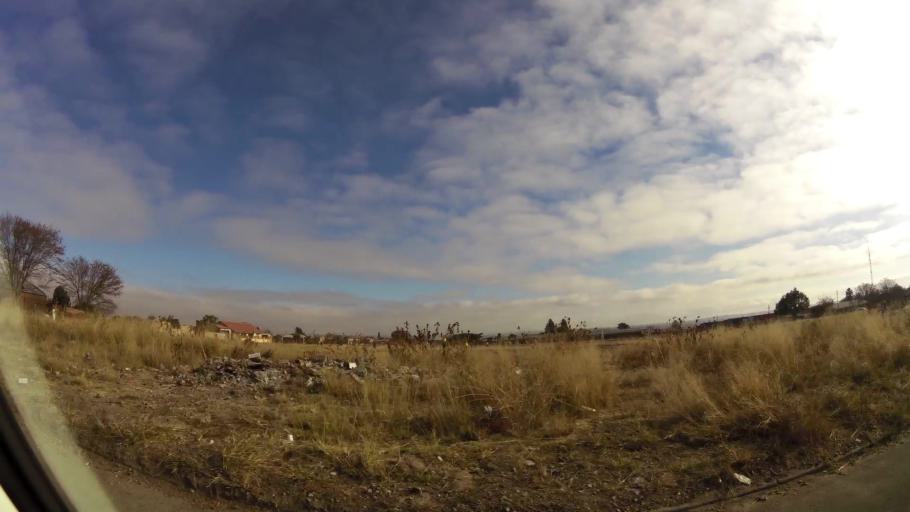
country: ZA
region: Limpopo
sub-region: Capricorn District Municipality
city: Polokwane
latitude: -23.8437
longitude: 29.3860
